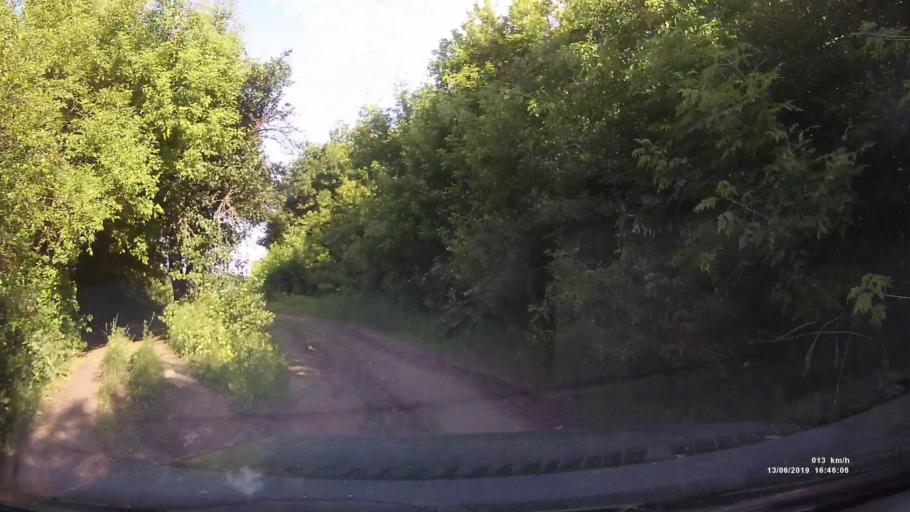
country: RU
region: Rostov
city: Kazanskaya
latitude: 49.9463
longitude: 41.4257
